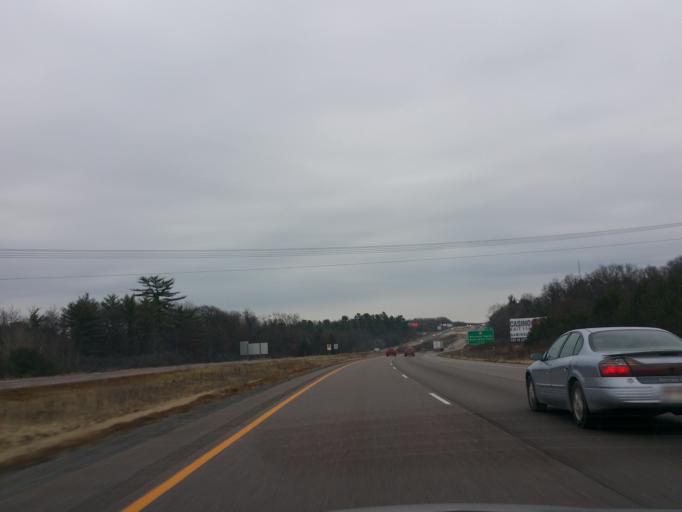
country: US
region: Wisconsin
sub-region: Jackson County
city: Black River Falls
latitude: 44.3078
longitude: -90.8386
